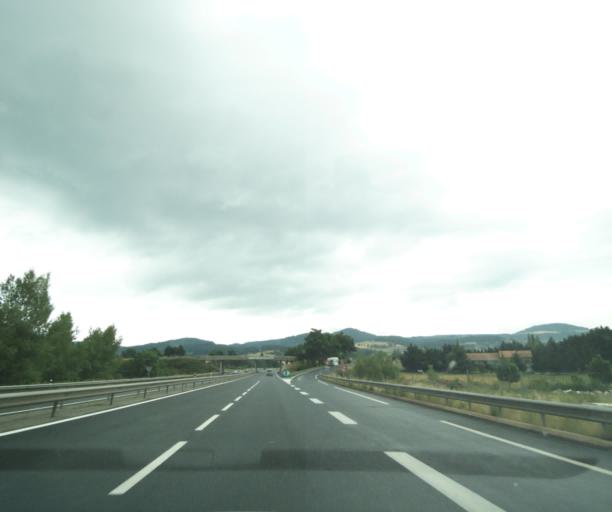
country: FR
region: Auvergne
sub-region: Departement de la Haute-Loire
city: Saint-Germain-Laprade
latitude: 45.0558
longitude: 3.9584
